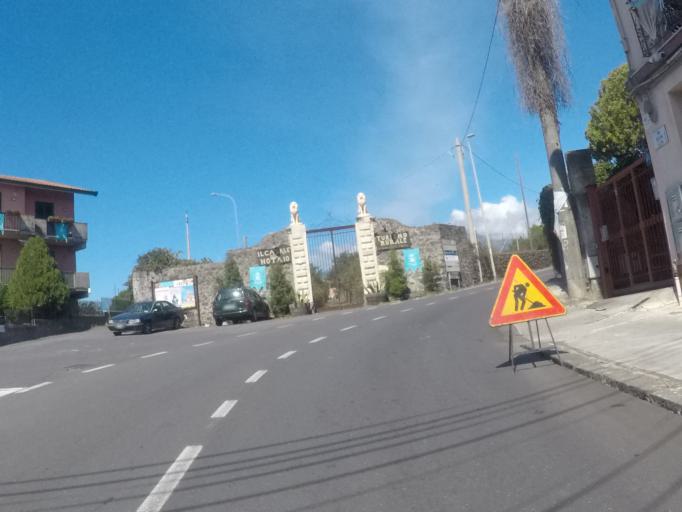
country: IT
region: Sicily
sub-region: Catania
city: Belpasso
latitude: 37.6057
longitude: 14.9846
